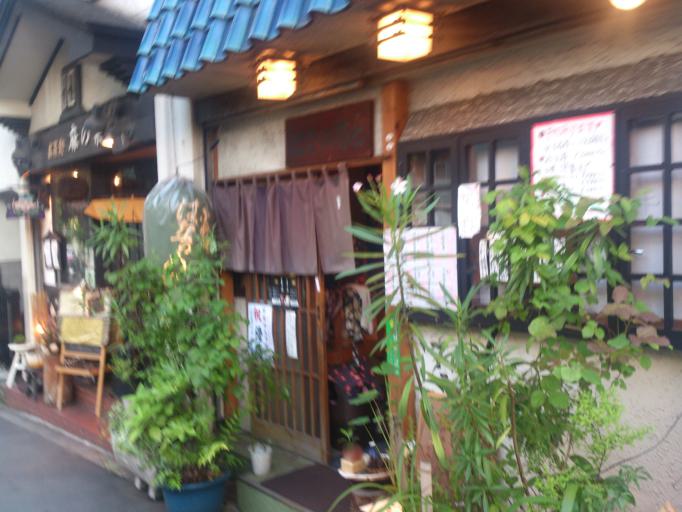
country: JP
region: Tokyo
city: Tokyo
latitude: 35.7075
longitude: 139.7178
